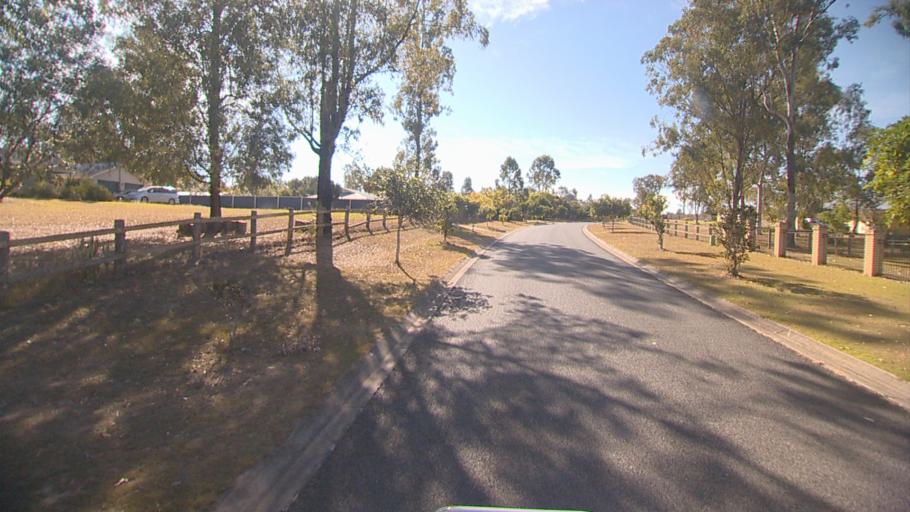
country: AU
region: Queensland
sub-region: Logan
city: North Maclean
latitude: -27.8045
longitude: 152.9661
